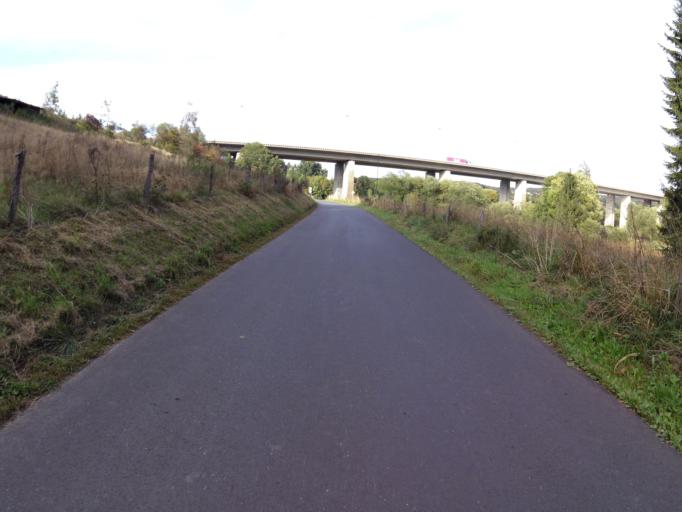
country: BE
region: Wallonia
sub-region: Province de Liege
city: Saint-Vith
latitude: 50.2595
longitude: 6.1453
